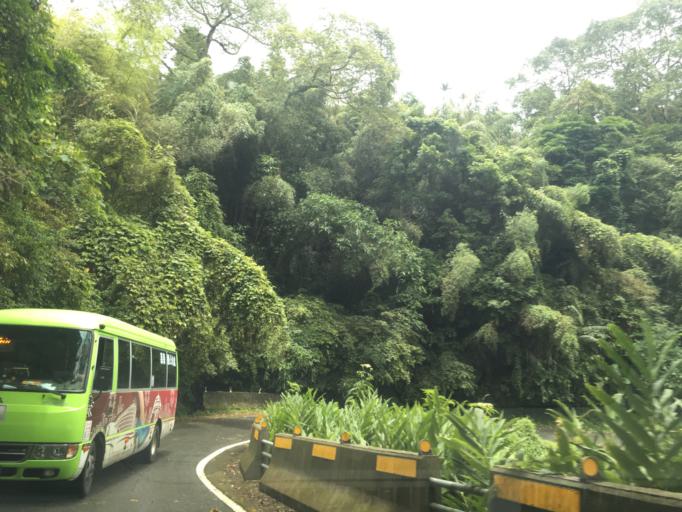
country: TW
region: Taiwan
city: Lugu
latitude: 23.5487
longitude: 120.6824
